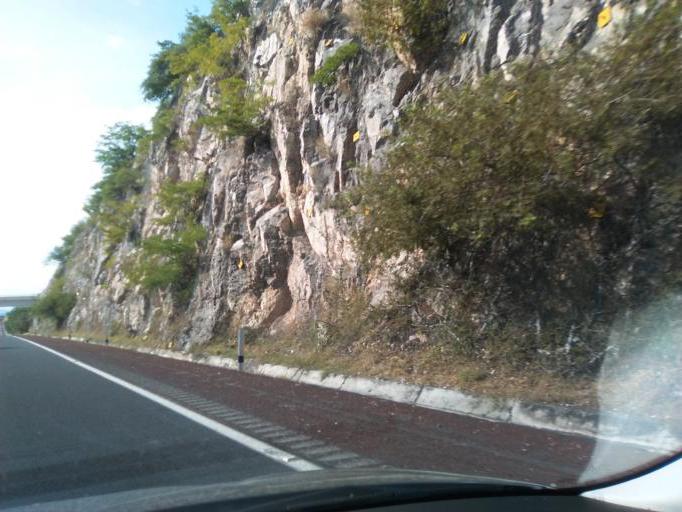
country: MX
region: Morelos
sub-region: Jojutla
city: Tehuixtla
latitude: 18.5932
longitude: -99.2678
